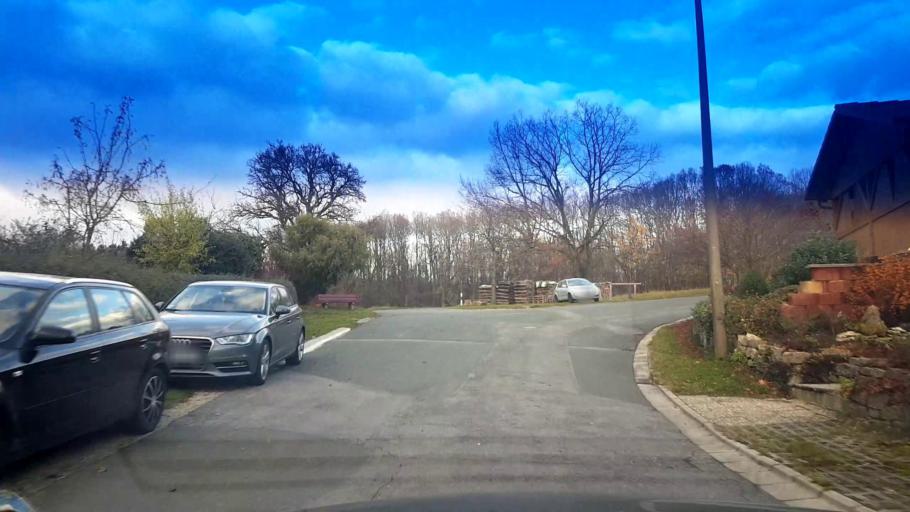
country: DE
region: Bavaria
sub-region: Upper Franconia
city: Schesslitz
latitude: 49.9714
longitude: 11.0638
